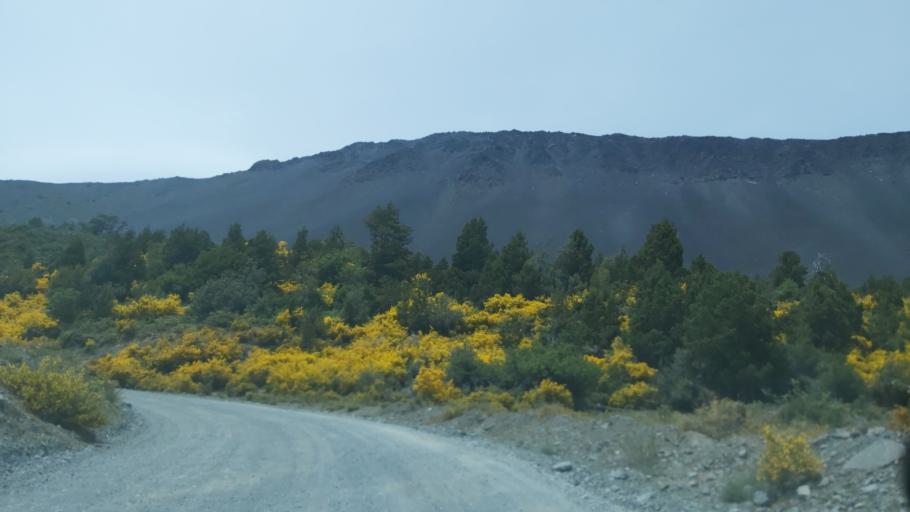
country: AR
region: Neuquen
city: Andacollo
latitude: -37.3930
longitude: -71.4066
